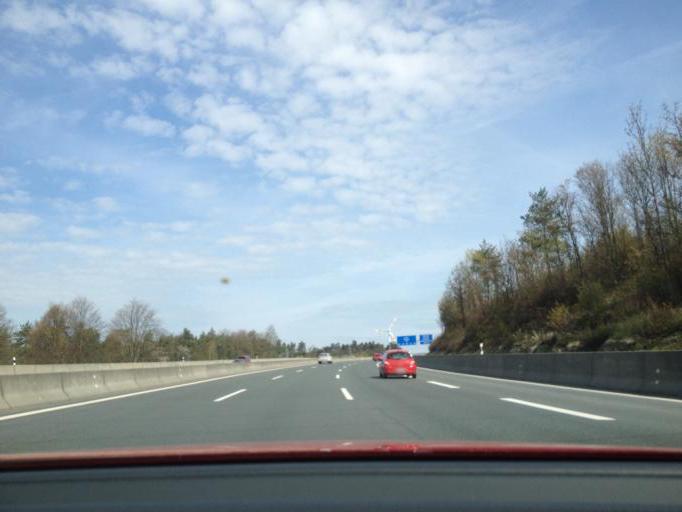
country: DE
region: Bavaria
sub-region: Upper Franconia
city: Bindlach
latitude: 50.0097
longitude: 11.6082
